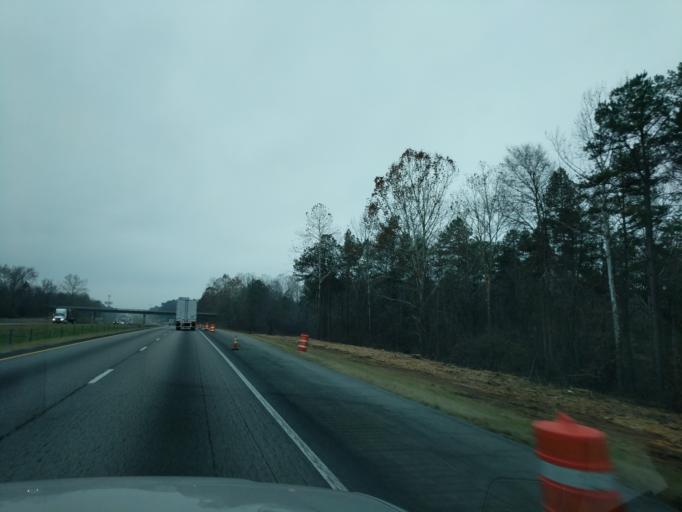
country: US
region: Georgia
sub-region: Banks County
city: Maysville
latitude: 34.1972
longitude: -83.5732
